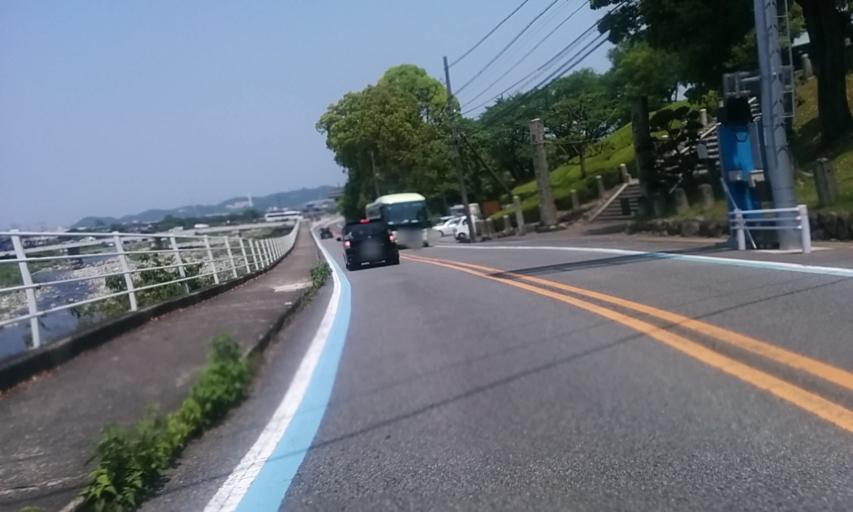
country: JP
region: Ehime
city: Niihama
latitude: 33.9212
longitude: 133.3087
